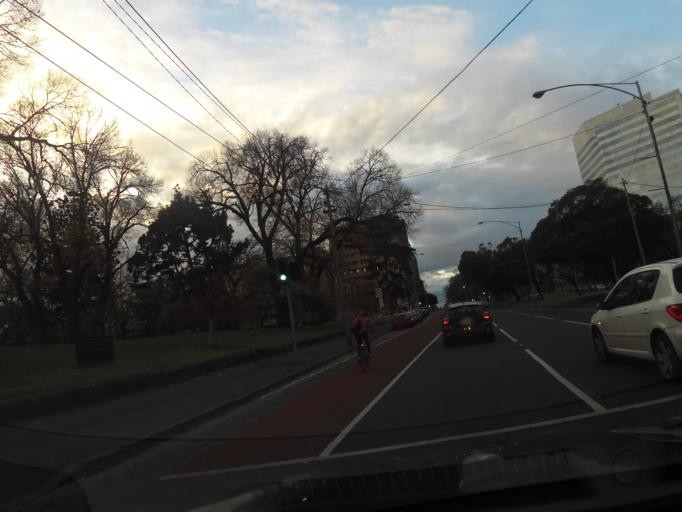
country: AU
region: Victoria
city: Carlton
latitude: -37.8075
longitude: 144.9712
